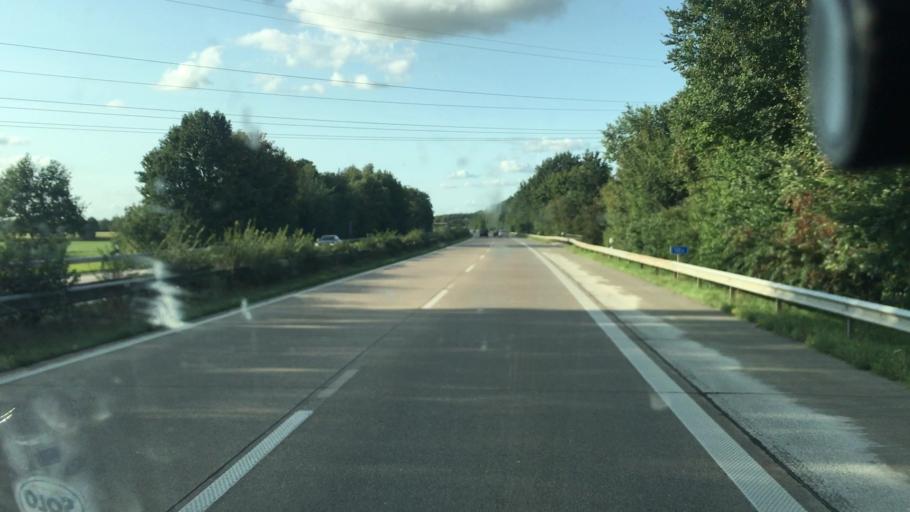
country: DE
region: Lower Saxony
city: Rastede
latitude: 53.2522
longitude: 8.1736
